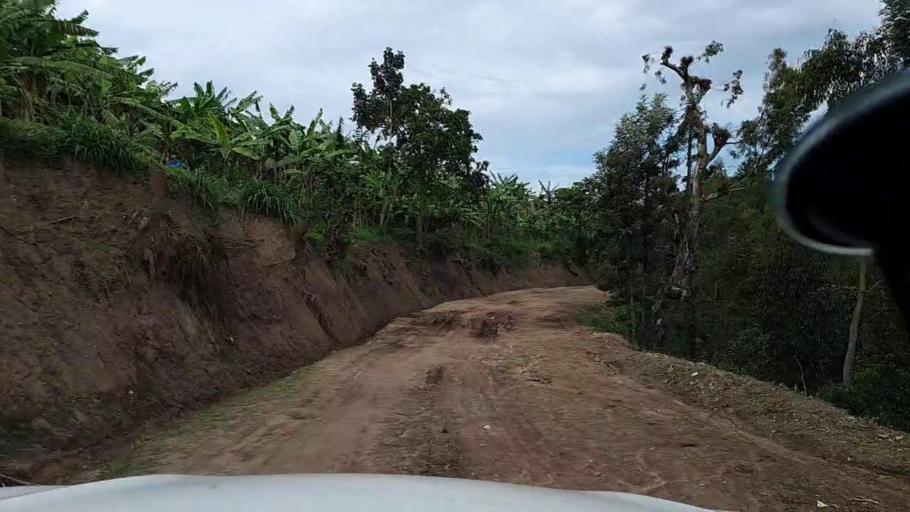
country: RW
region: Southern Province
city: Gitarama
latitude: -2.1285
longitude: 29.6575
